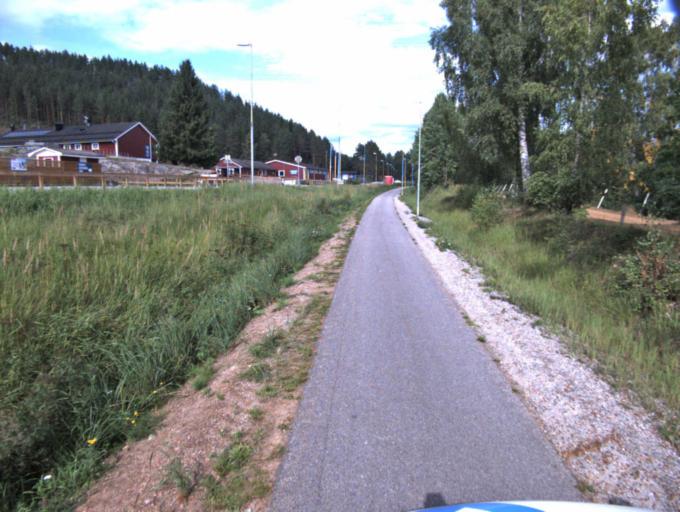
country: SE
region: Vaestra Goetaland
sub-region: Ulricehamns Kommun
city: Ulricehamn
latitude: 57.8191
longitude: 13.4125
